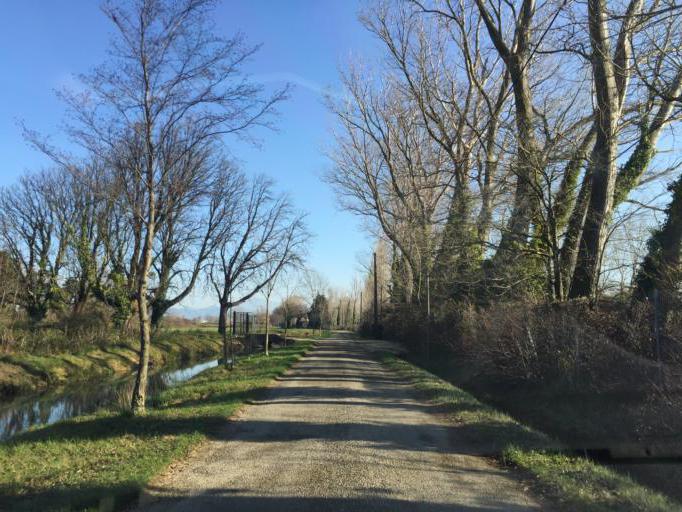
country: FR
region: Provence-Alpes-Cote d'Azur
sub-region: Departement du Vaucluse
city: Orange
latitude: 44.1266
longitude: 4.8489
